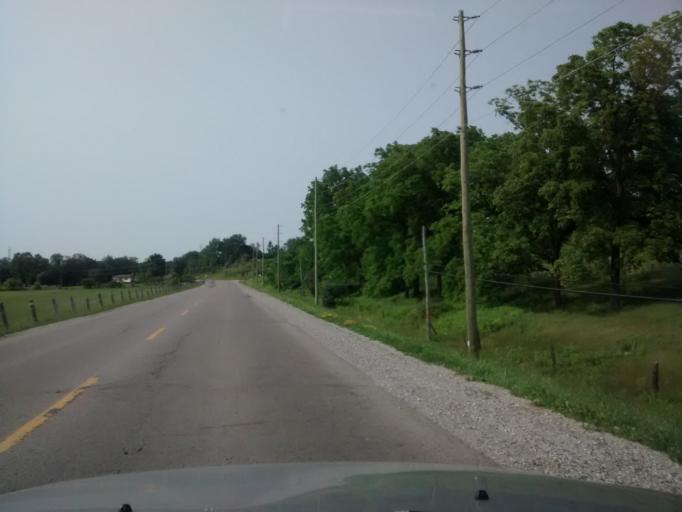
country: CA
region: Ontario
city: Ancaster
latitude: 43.0547
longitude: -79.9135
